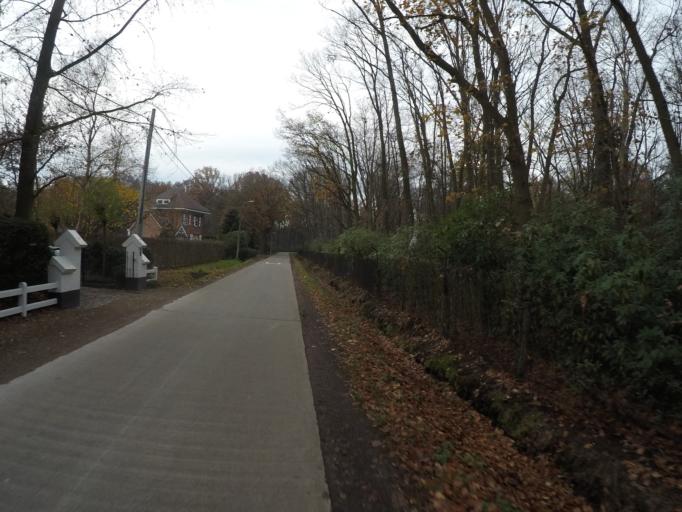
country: BE
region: Flanders
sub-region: Provincie Antwerpen
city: Heist-op-den-Berg
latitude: 51.1013
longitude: 4.7093
